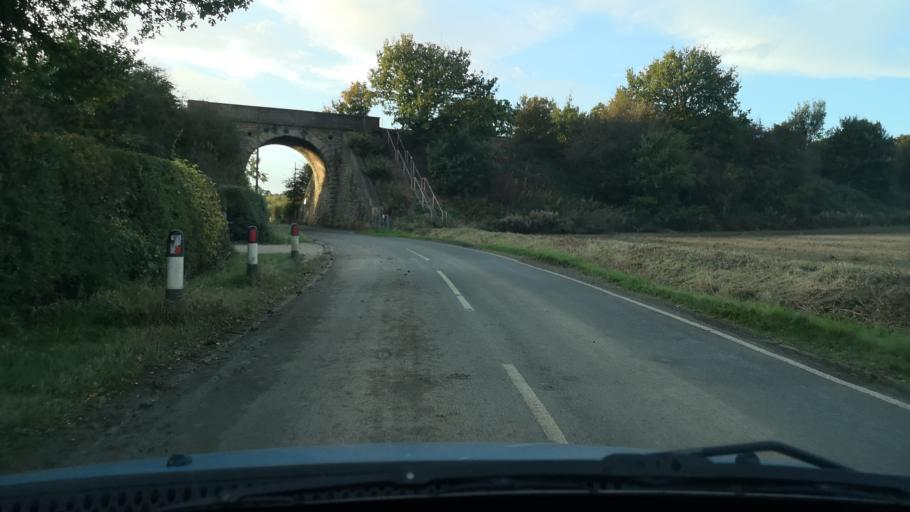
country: GB
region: England
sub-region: City and Borough of Wakefield
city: Low Ackworth
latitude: 53.6507
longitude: -1.3131
